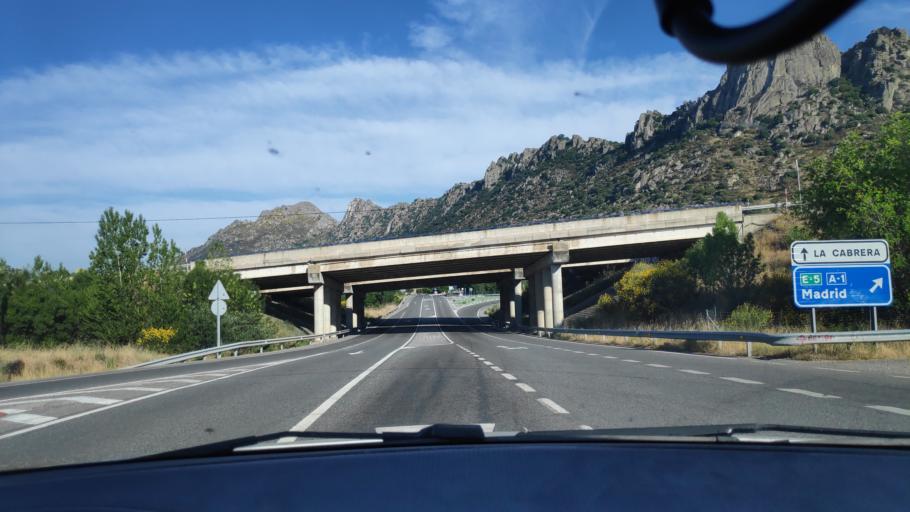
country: ES
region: Madrid
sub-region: Provincia de Madrid
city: La Cabrera
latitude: 40.8738
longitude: -3.6008
